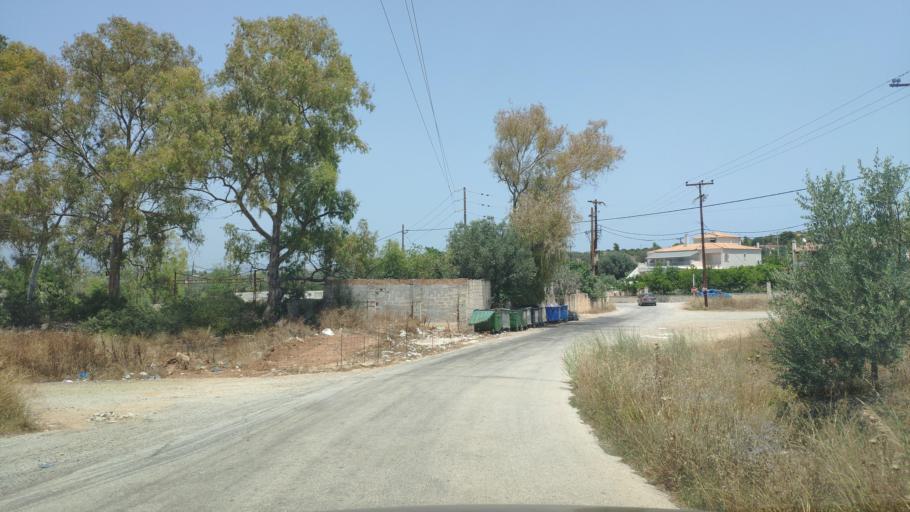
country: GR
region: Peloponnese
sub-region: Nomos Argolidos
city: Porto Cheli
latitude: 37.3109
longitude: 23.1575
